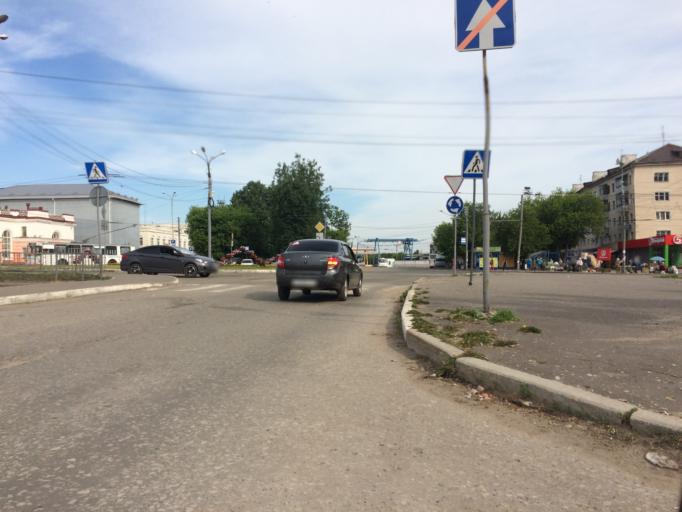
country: RU
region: Mariy-El
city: Yoshkar-Ola
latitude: 56.6218
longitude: 47.8816
